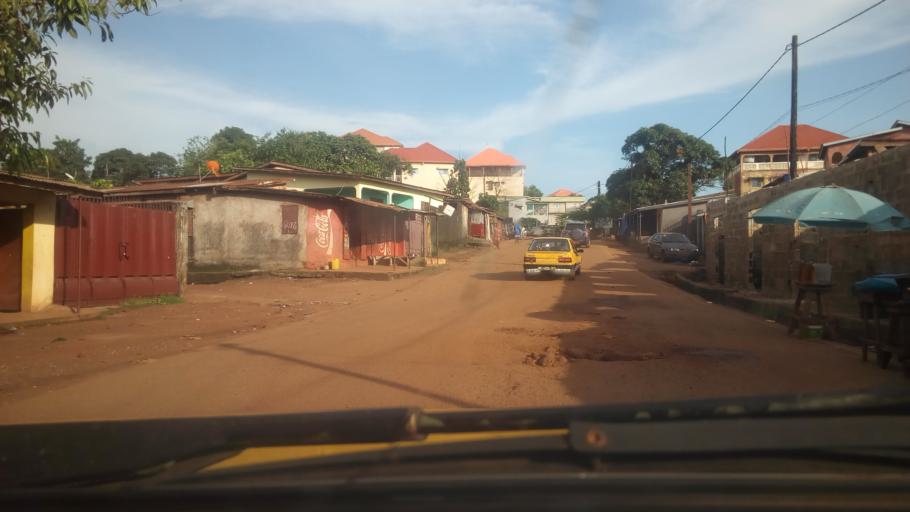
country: GN
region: Conakry
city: Conakry
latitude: 9.6231
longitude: -13.6118
